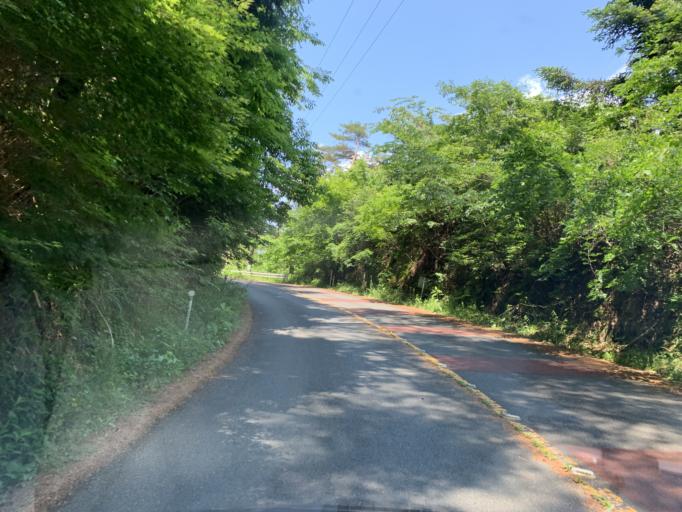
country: JP
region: Miyagi
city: Matsushima
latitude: 38.3574
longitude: 141.0579
